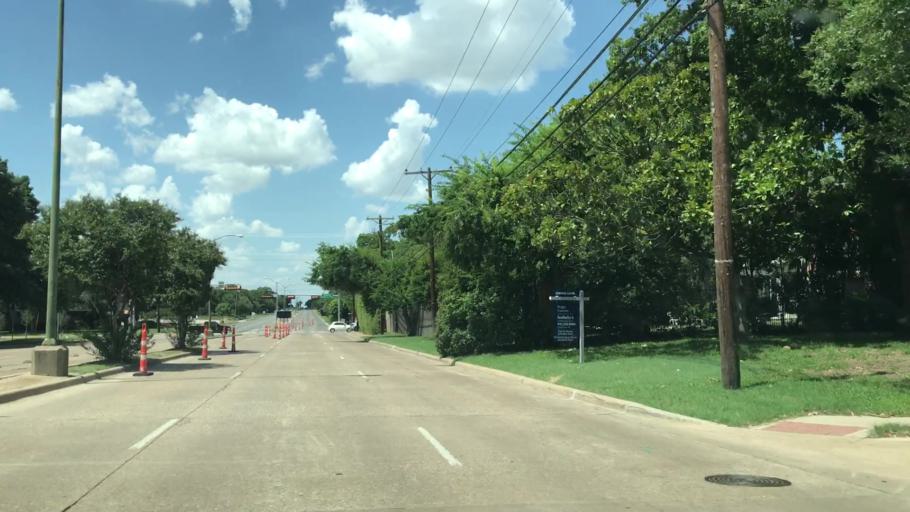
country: US
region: Texas
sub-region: Dallas County
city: University Park
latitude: 32.8939
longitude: -96.8383
